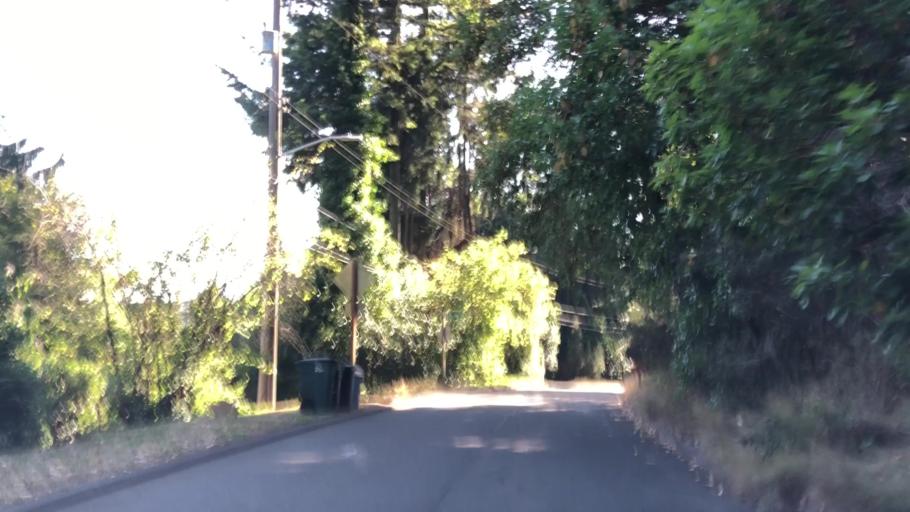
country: US
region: Washington
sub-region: King County
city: Lake Forest Park
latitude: 47.7571
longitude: -122.2739
